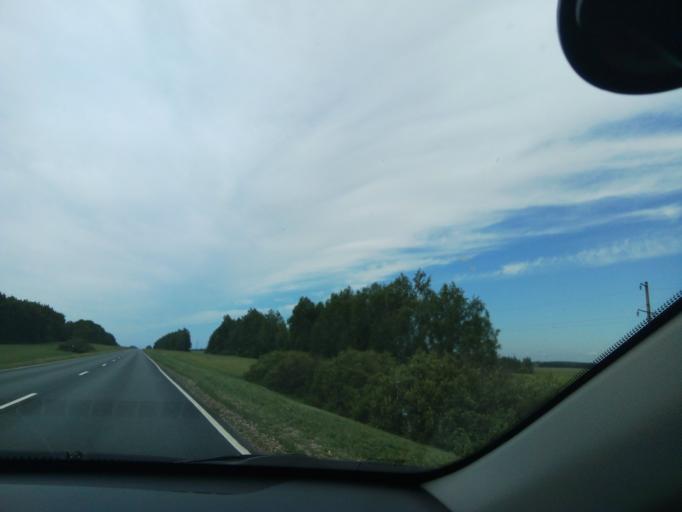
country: RU
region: Tambov
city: Selezni
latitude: 52.6413
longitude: 40.9697
